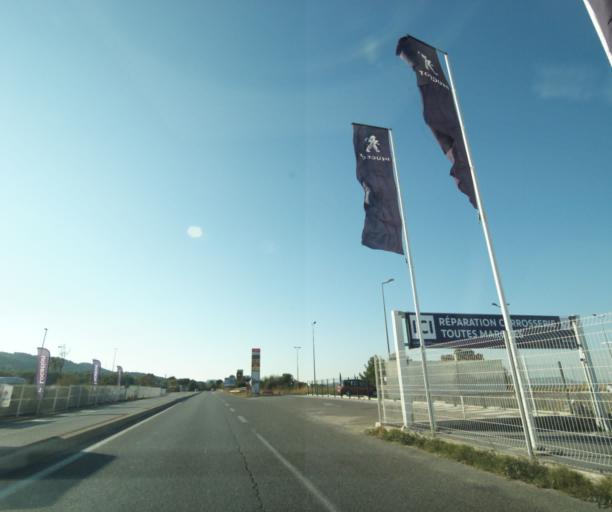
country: FR
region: Provence-Alpes-Cote d'Azur
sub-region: Departement des Bouches-du-Rhone
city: Chateauneuf-les-Martigues
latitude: 43.3944
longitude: 5.1351
